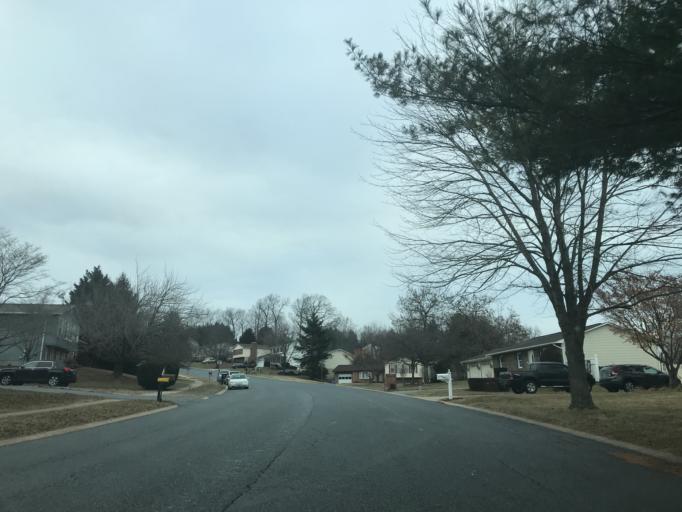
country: US
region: Maryland
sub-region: Carroll County
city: Eldersburg
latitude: 39.4038
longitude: -76.9209
